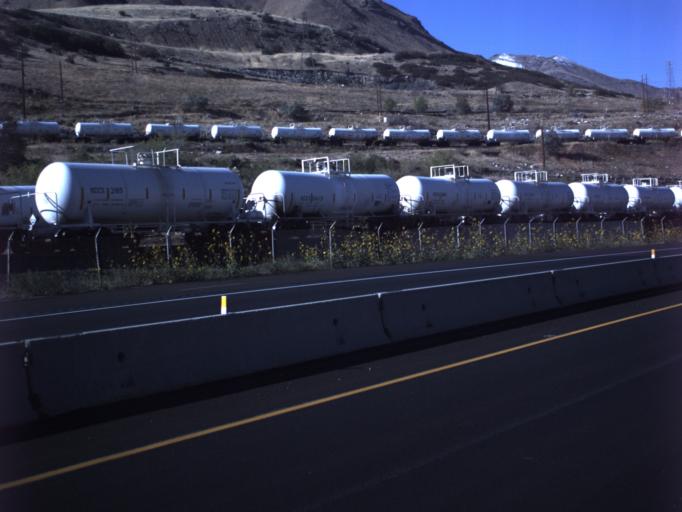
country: US
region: Utah
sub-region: Salt Lake County
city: Magna
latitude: 40.7193
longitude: -112.1452
